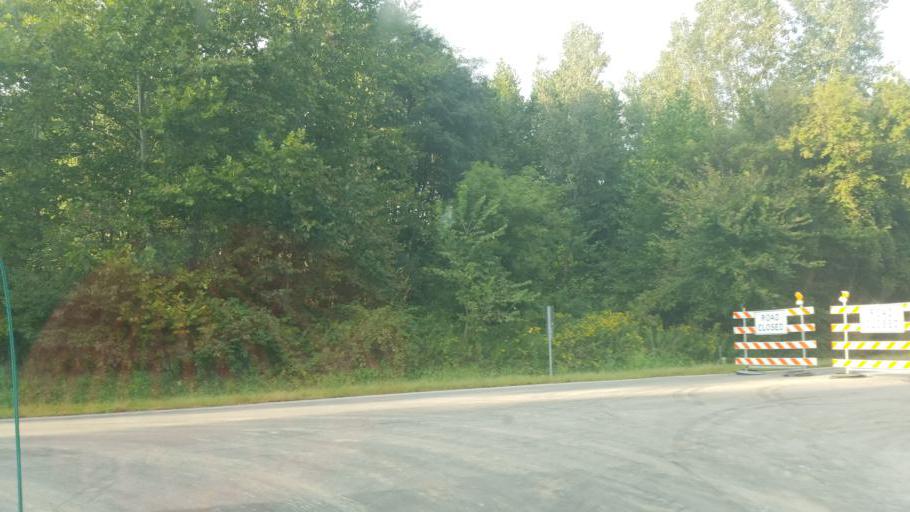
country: US
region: Ohio
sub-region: Wayne County
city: Shreve
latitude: 40.7487
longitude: -82.1287
